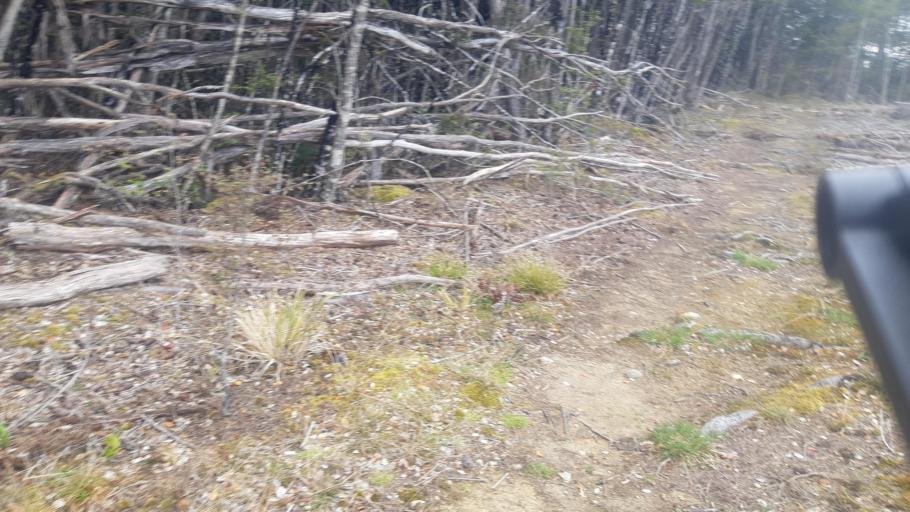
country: NZ
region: Tasman
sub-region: Tasman District
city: Wakefield
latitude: -41.7648
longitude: 172.8129
